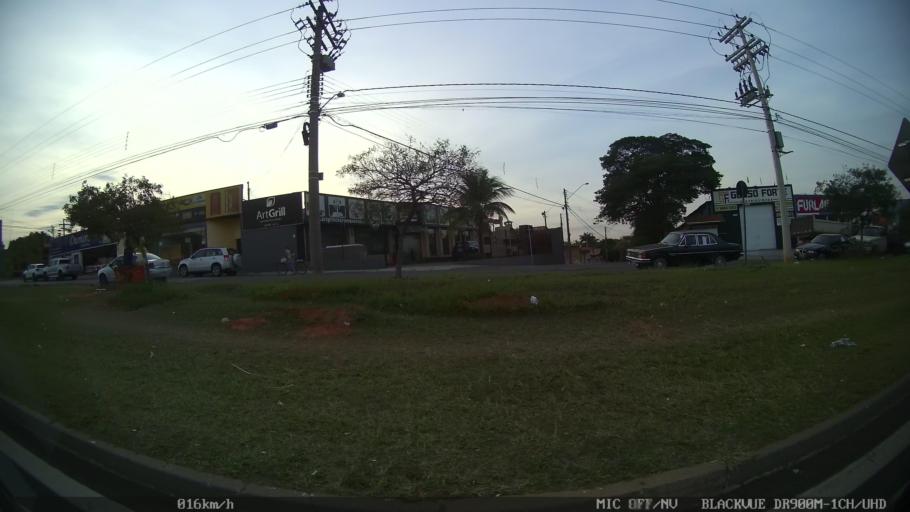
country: BR
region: Sao Paulo
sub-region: Limeira
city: Limeira
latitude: -22.5622
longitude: -47.4209
